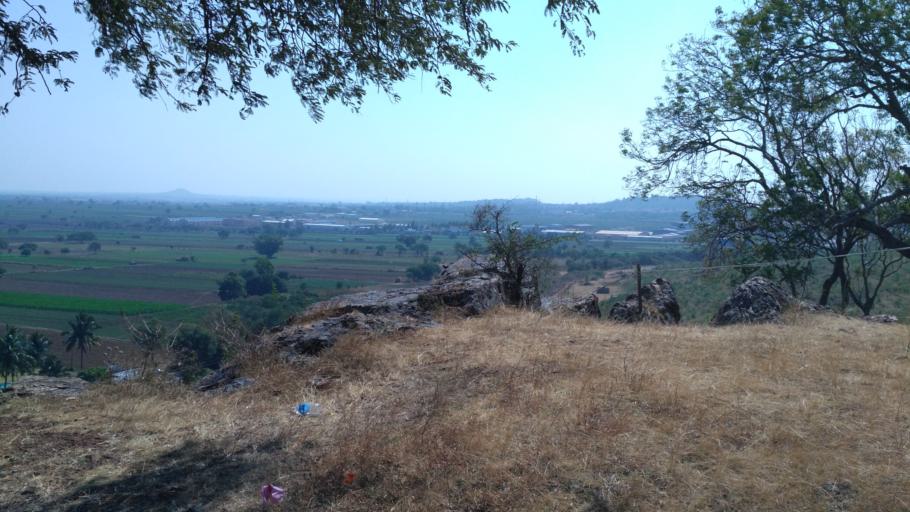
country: IN
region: Karnataka
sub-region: Dharwad
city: Hubli
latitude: 15.4276
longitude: 75.0548
